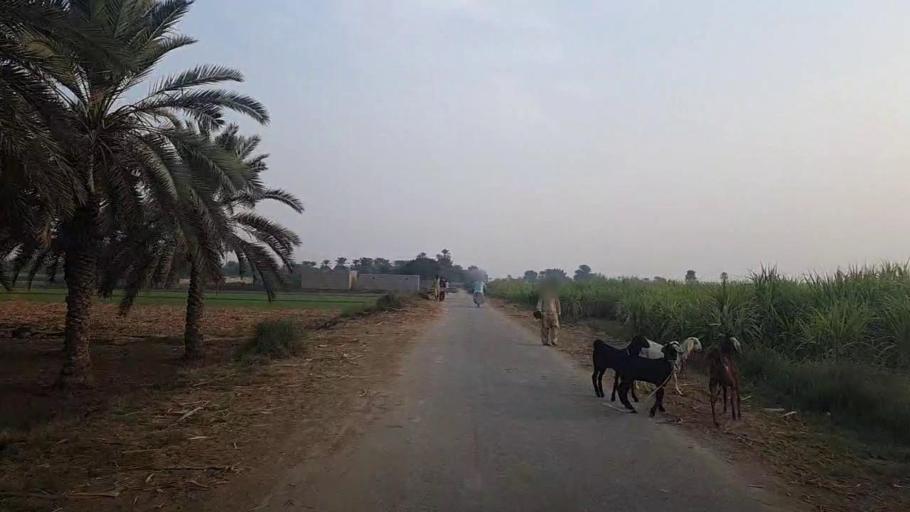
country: PK
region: Sindh
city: Kot Diji
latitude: 27.3815
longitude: 68.6633
